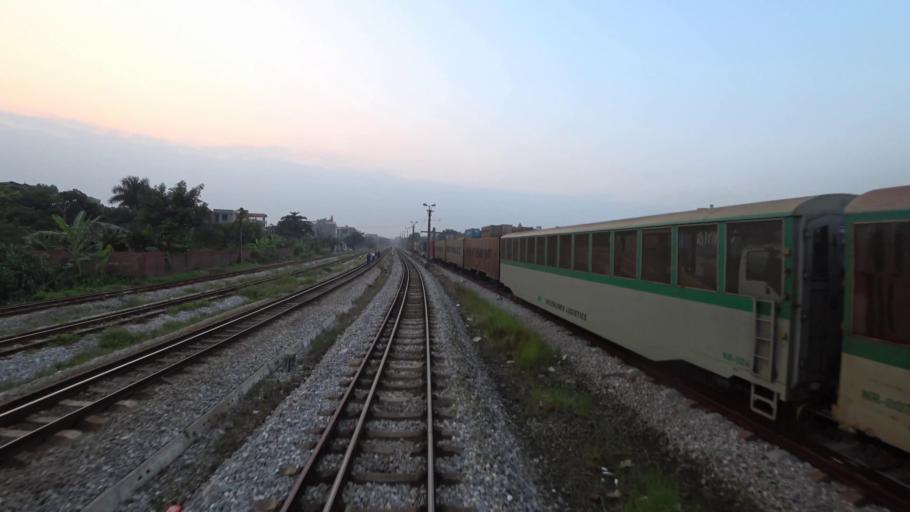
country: VN
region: Ha Noi
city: Dong Anh
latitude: 21.1528
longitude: 105.8529
